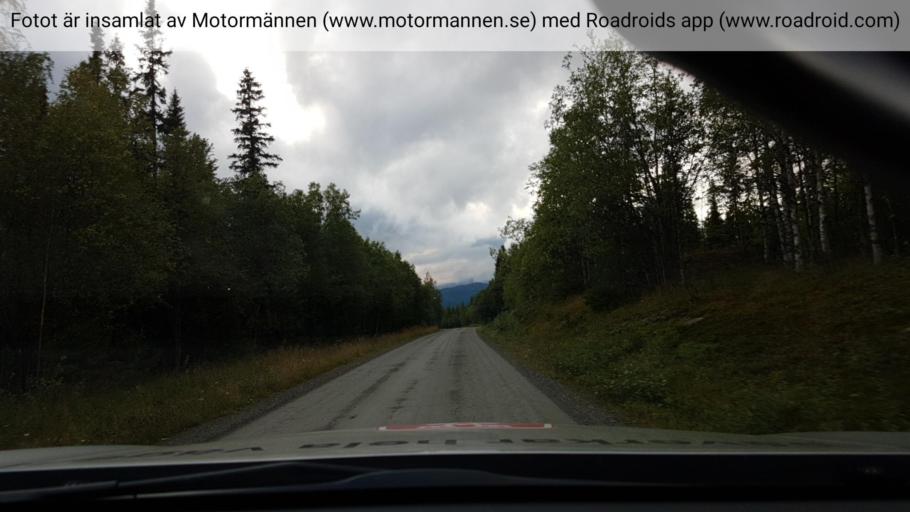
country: SE
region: Vaesterbotten
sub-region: Vilhelmina Kommun
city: Sjoberg
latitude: 65.5088
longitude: 15.6382
